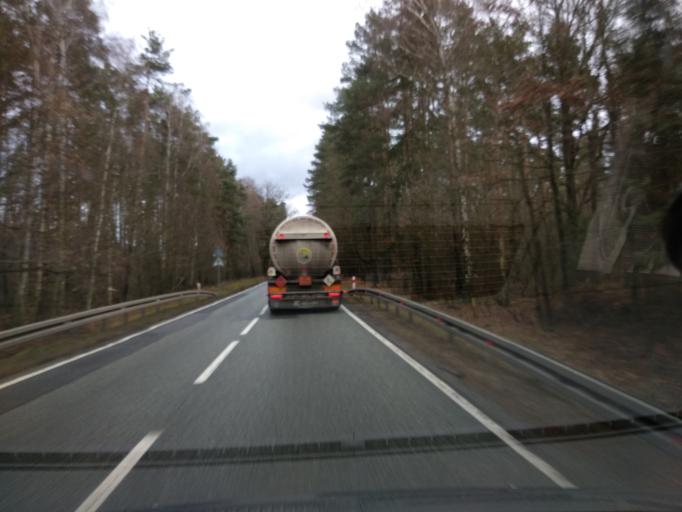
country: PL
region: Lower Silesian Voivodeship
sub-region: Powiat olesnicki
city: Twardogora
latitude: 51.3024
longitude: 17.5374
